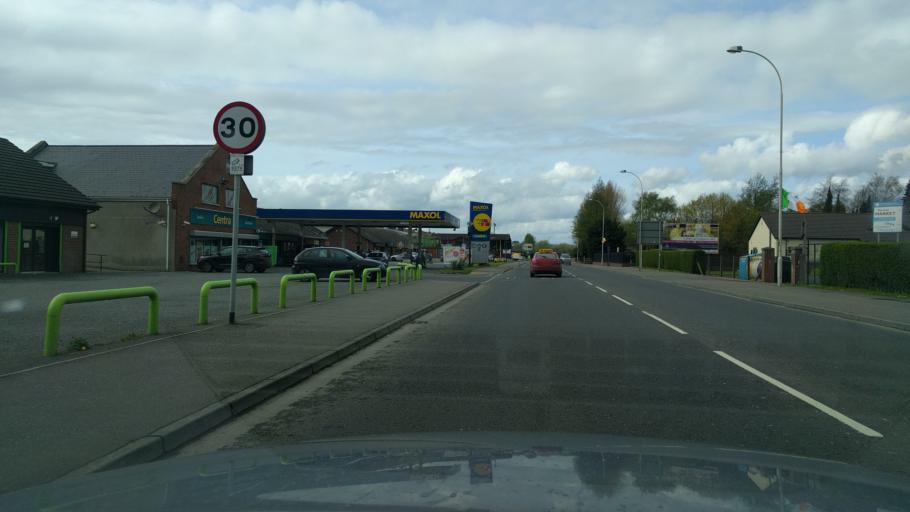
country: GB
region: Northern Ireland
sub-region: Newry and Mourne District
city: Newry
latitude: 54.1650
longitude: -6.3327
